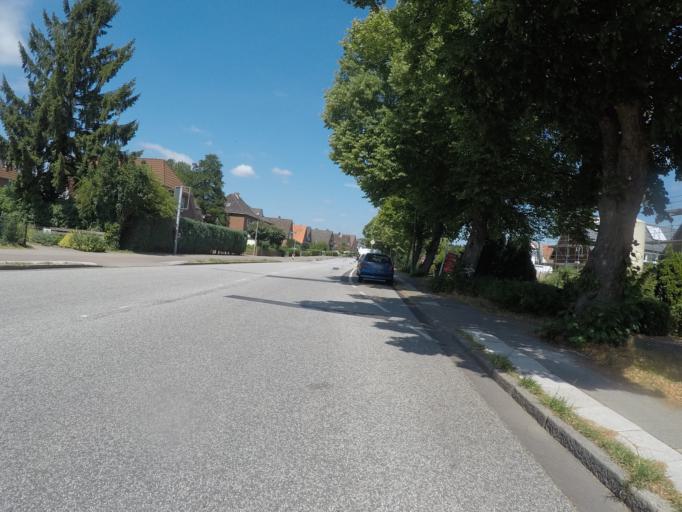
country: DE
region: Hamburg
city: Harburg
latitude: 53.4916
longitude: 10.0187
